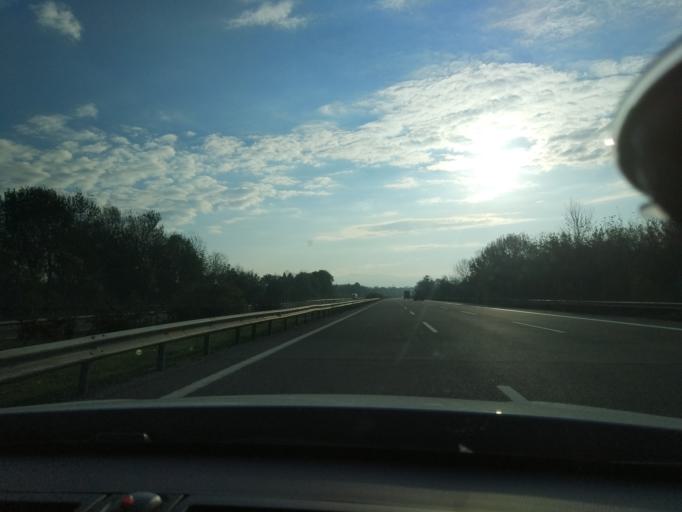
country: TR
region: Duzce
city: Duzce
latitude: 40.8043
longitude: 31.1645
